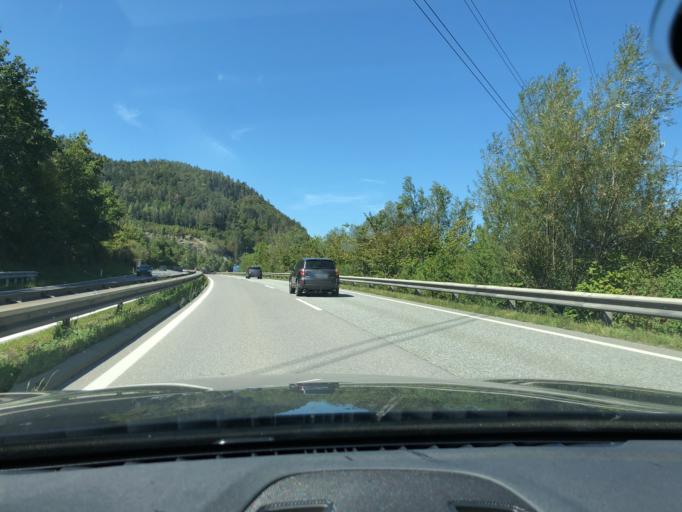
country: AT
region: Vorarlberg
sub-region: Politischer Bezirk Bludenz
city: Nuziders
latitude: 47.1586
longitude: 9.8036
